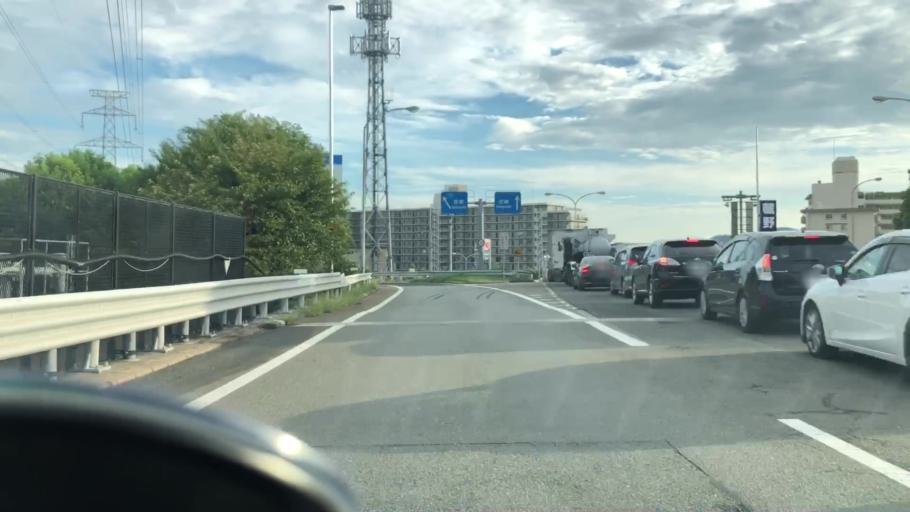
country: JP
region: Hyogo
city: Takarazuka
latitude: 34.8034
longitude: 135.3675
